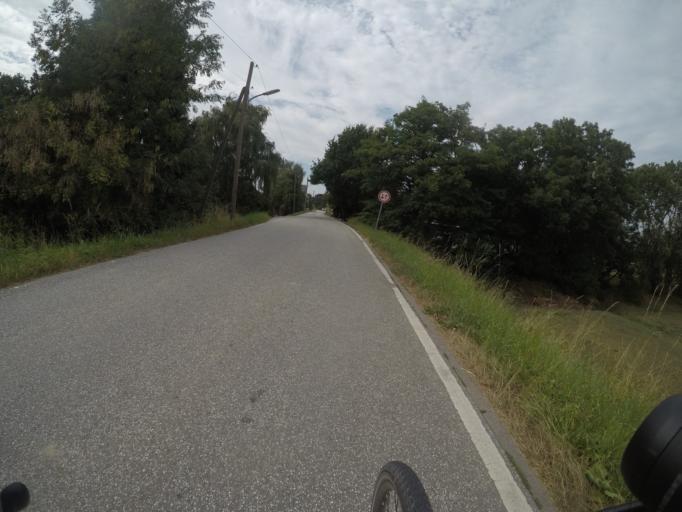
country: DE
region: Schleswig-Holstein
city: Oststeinbek
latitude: 53.4765
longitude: 10.1347
